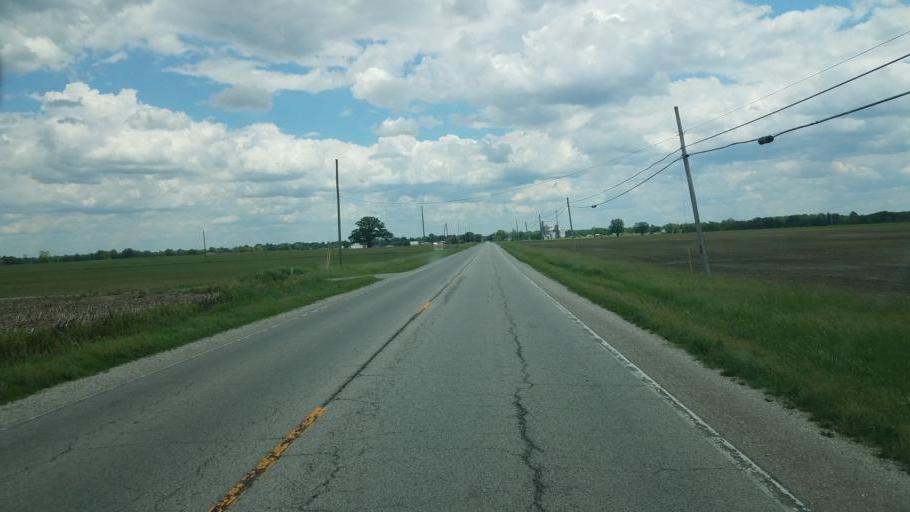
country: US
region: Ohio
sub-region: Crawford County
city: Bucyrus
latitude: 40.8168
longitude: -83.0085
